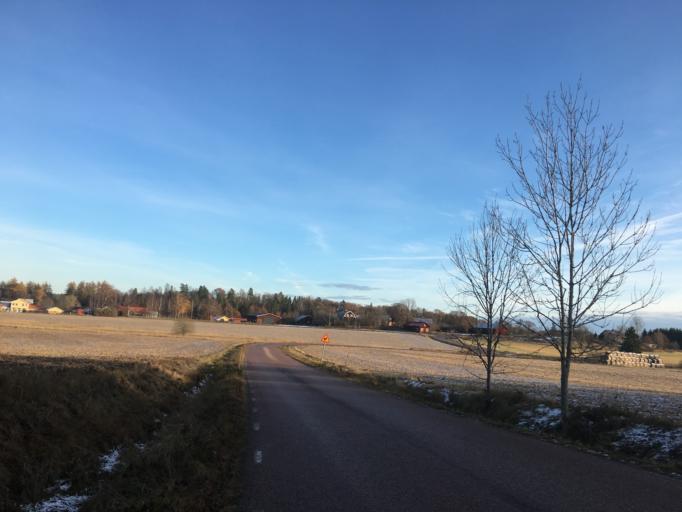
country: SE
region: Vaestmanland
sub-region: Vasteras
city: Vasteras
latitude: 59.6422
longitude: 16.4755
